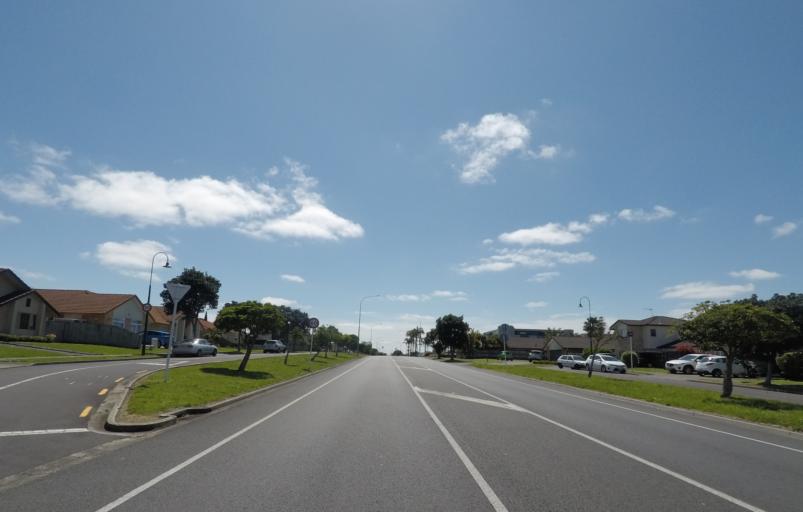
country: NZ
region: Auckland
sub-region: Auckland
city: Manukau City
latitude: -36.9510
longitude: 174.9104
